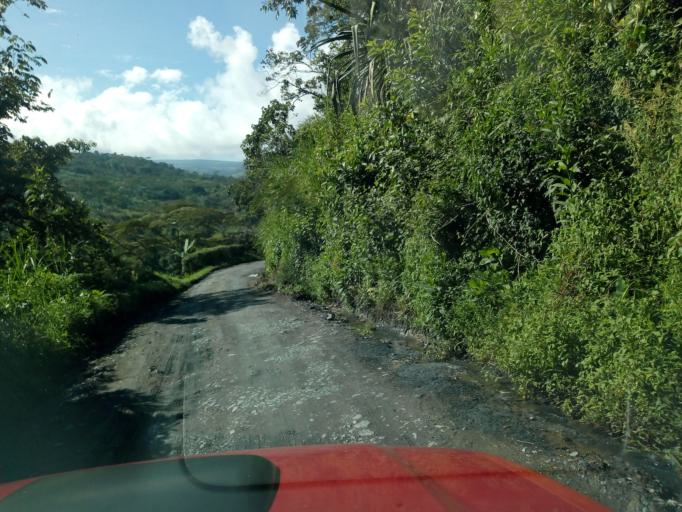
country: CO
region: Boyaca
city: Moniquira
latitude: 5.8945
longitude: -73.5314
